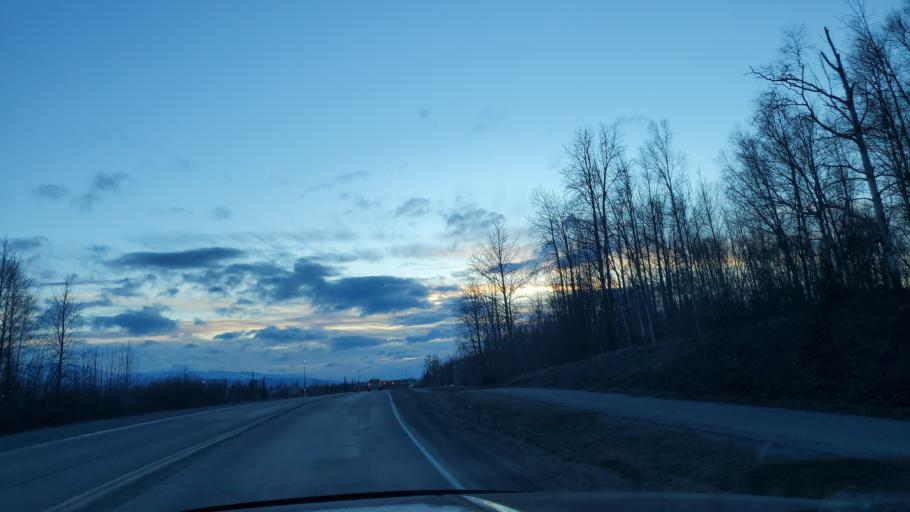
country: US
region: Alaska
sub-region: Matanuska-Susitna Borough
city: Wasilla
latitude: 61.5745
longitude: -149.4418
